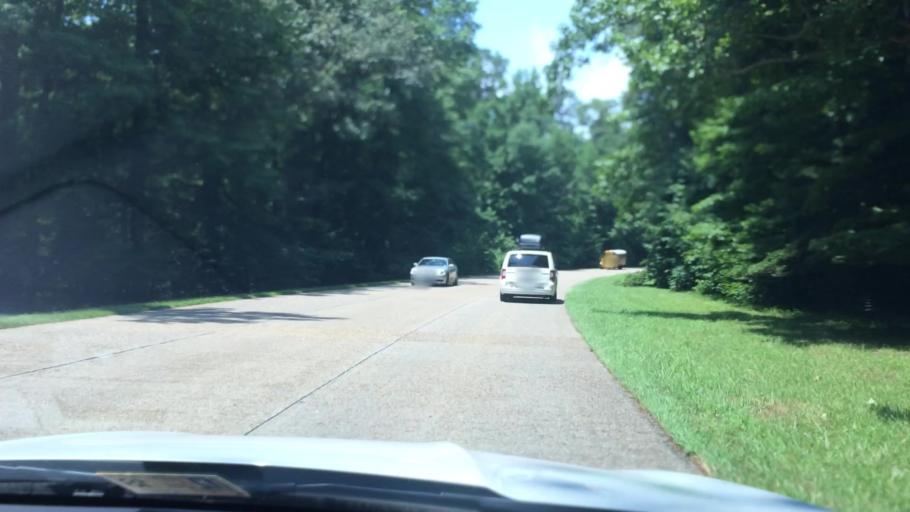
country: US
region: Virginia
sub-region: York County
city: Yorktown
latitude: 37.2304
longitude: -76.5202
